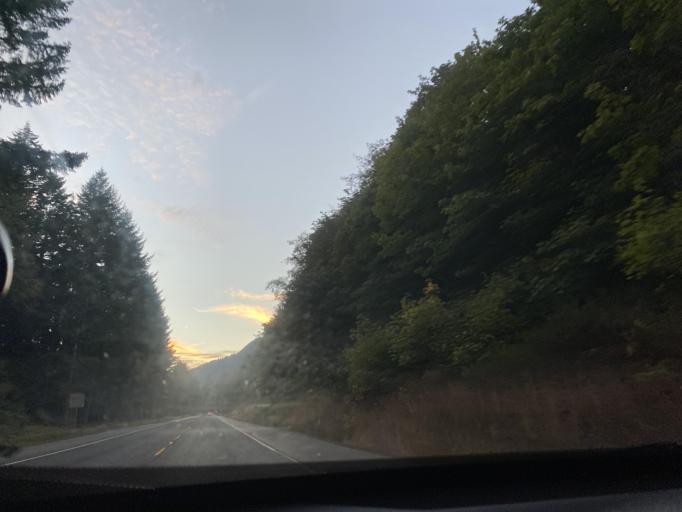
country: US
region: Washington
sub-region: Clallam County
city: Port Angeles
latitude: 48.0859
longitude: -123.7146
